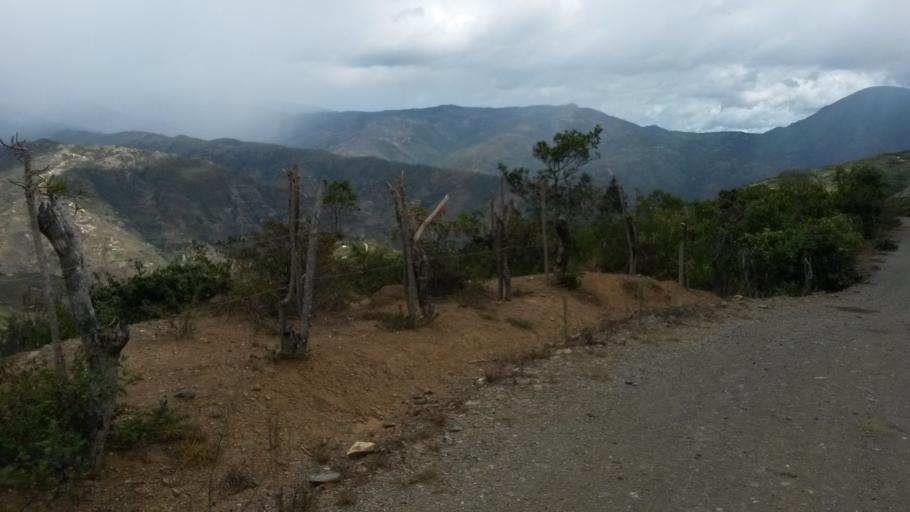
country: CO
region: Cauca
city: Almaguer
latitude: 1.8710
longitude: -76.8229
